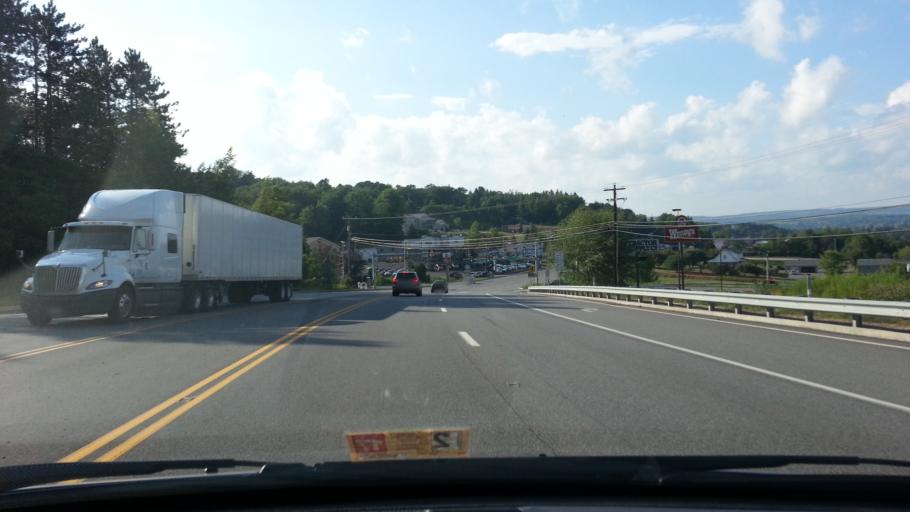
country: US
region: Pennsylvania
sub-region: Elk County
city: Saint Marys
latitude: 41.3997
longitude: -78.5591
